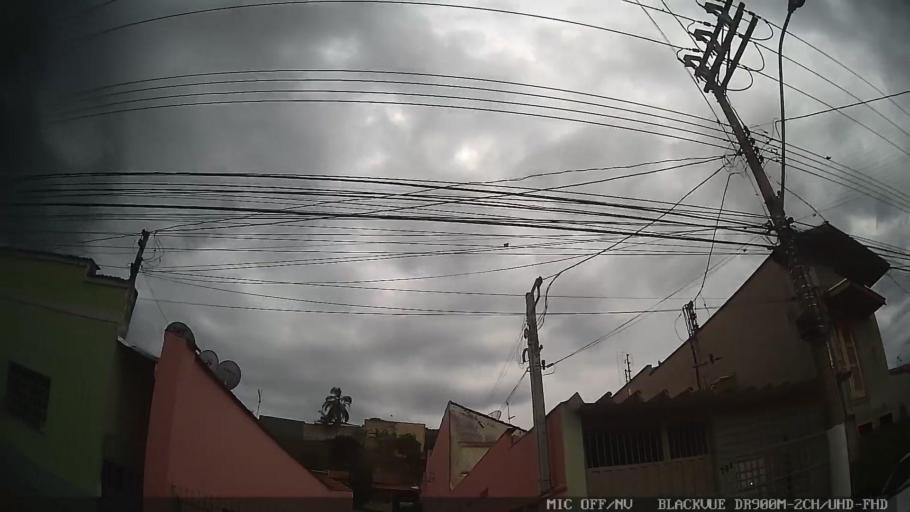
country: BR
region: Sao Paulo
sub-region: Amparo
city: Amparo
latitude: -22.7061
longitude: -46.7781
